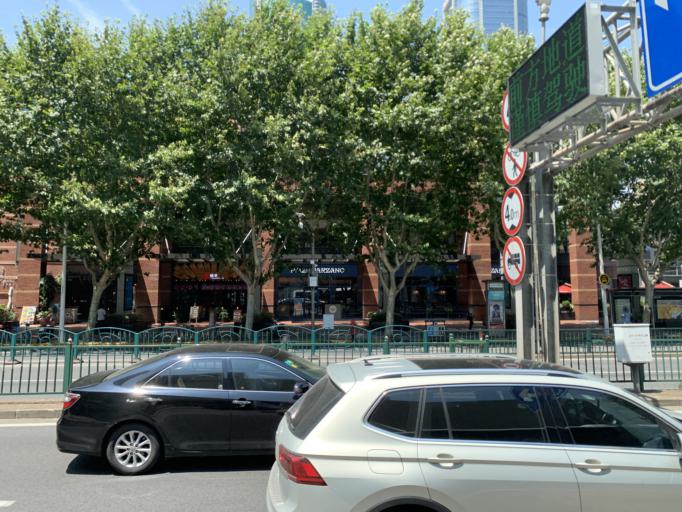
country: CN
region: Shanghai Shi
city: Pudong
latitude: 31.2297
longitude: 121.5216
